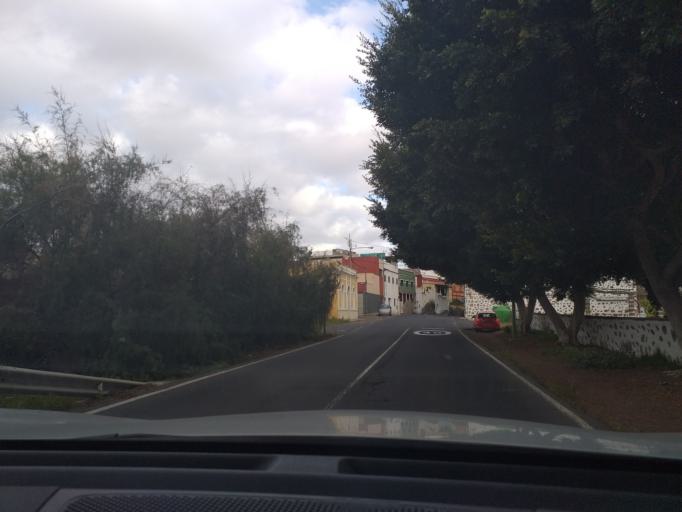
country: ES
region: Canary Islands
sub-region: Provincia de Las Palmas
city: Arucas
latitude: 28.1003
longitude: -15.4859
